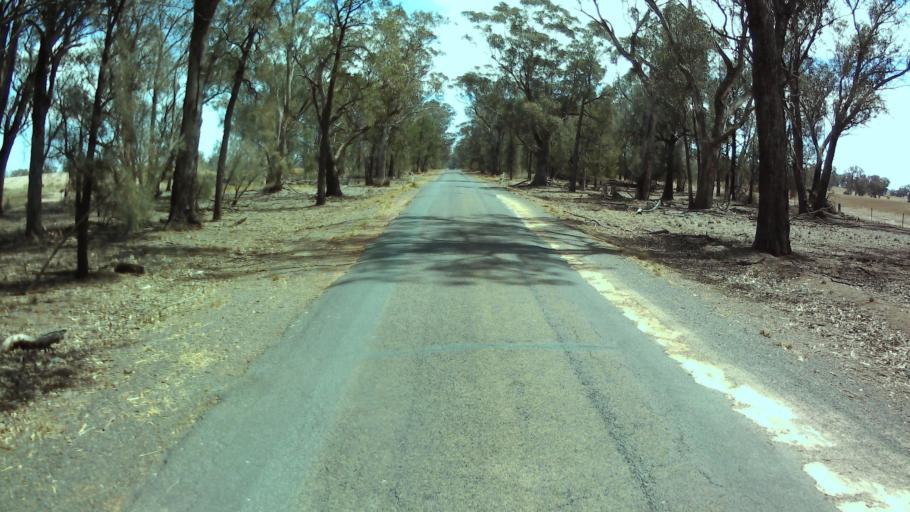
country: AU
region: New South Wales
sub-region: Weddin
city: Grenfell
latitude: -33.6525
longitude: 148.1957
